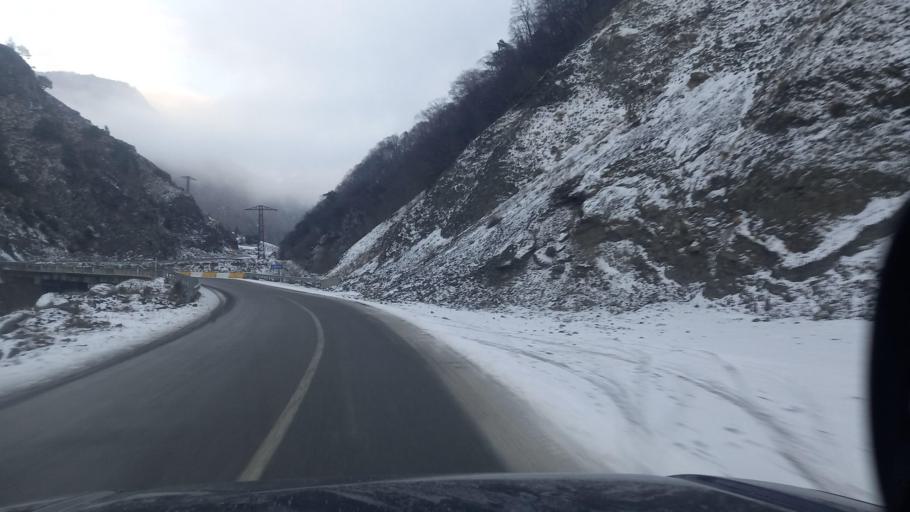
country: RU
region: Ingushetiya
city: Dzhayrakh
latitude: 42.7904
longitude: 44.7714
